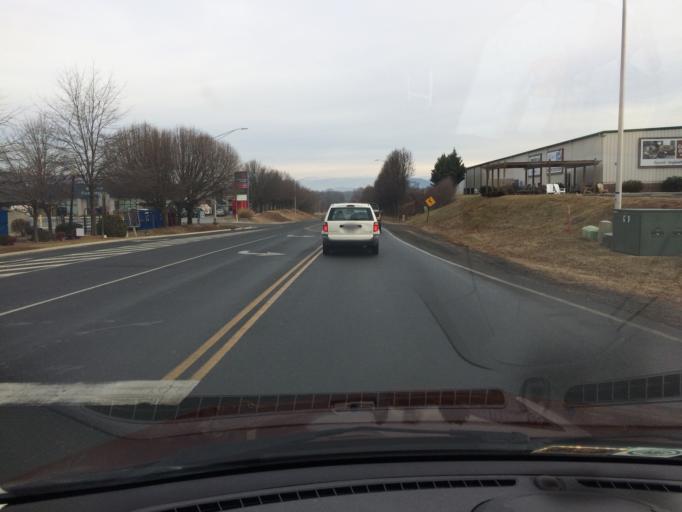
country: US
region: Virginia
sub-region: City of Bedford
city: Bedford
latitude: 37.3276
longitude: -79.5023
